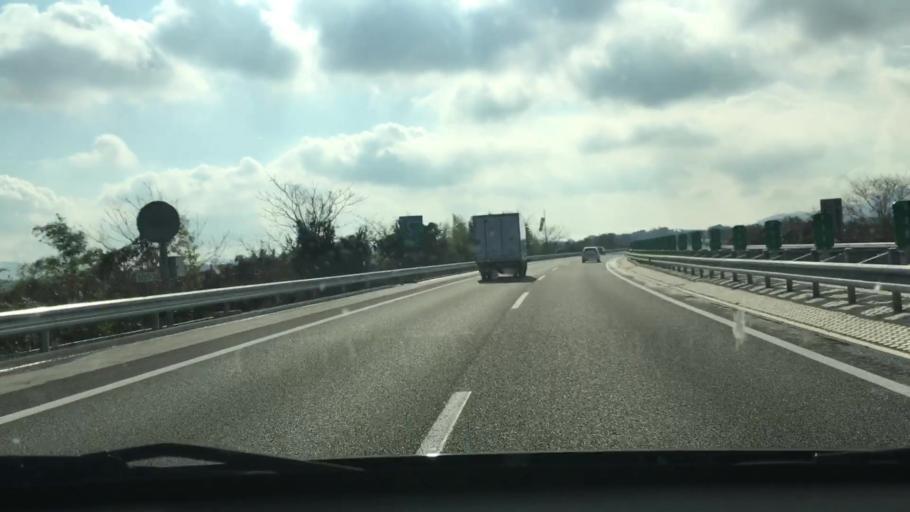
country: JP
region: Kumamoto
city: Uto
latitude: 32.7168
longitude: 130.7683
